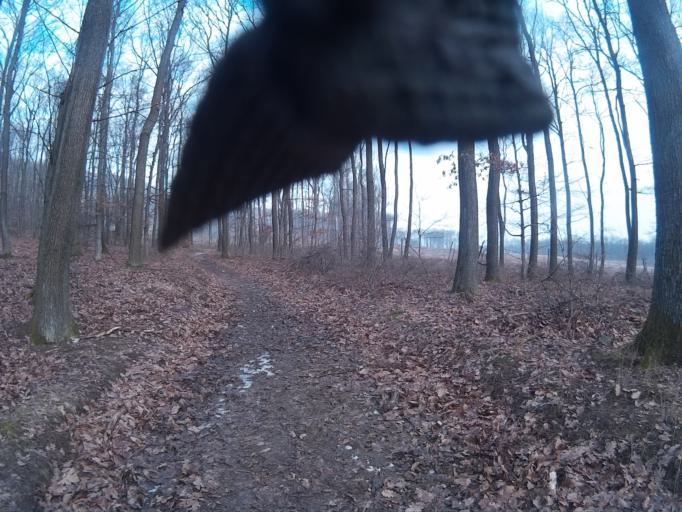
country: HU
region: Komarom-Esztergom
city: Tarjan
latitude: 47.6685
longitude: 18.5036
